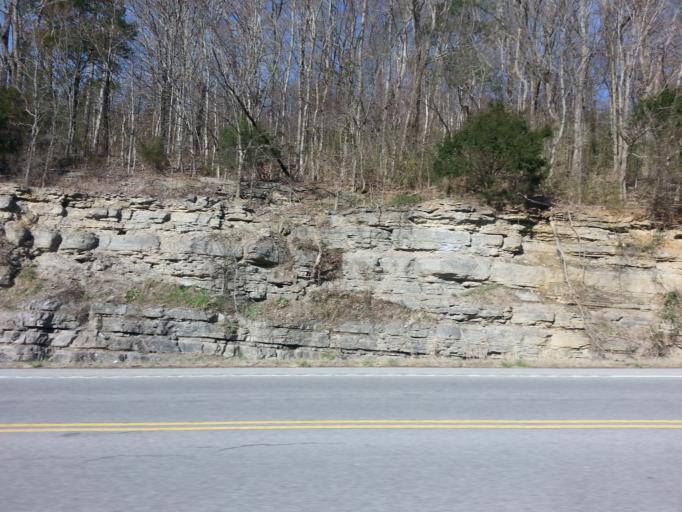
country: US
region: Tennessee
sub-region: Cannon County
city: Woodbury
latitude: 35.8199
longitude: -86.0382
